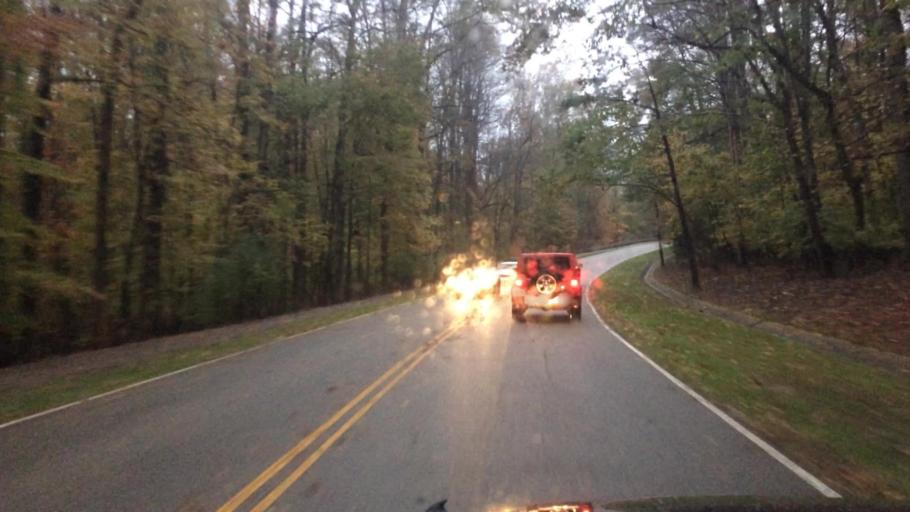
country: US
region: Virginia
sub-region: City of Williamsburg
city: Williamsburg
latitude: 37.2382
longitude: -76.6813
